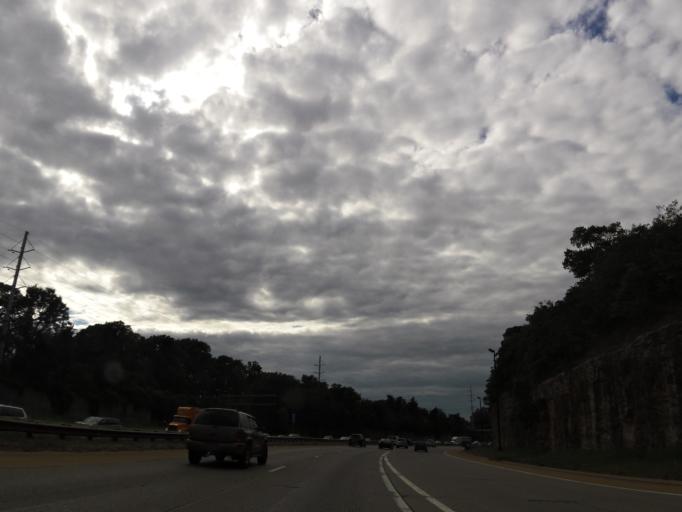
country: US
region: Tennessee
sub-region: Davidson County
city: Oak Hill
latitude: 36.1242
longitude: -86.8118
